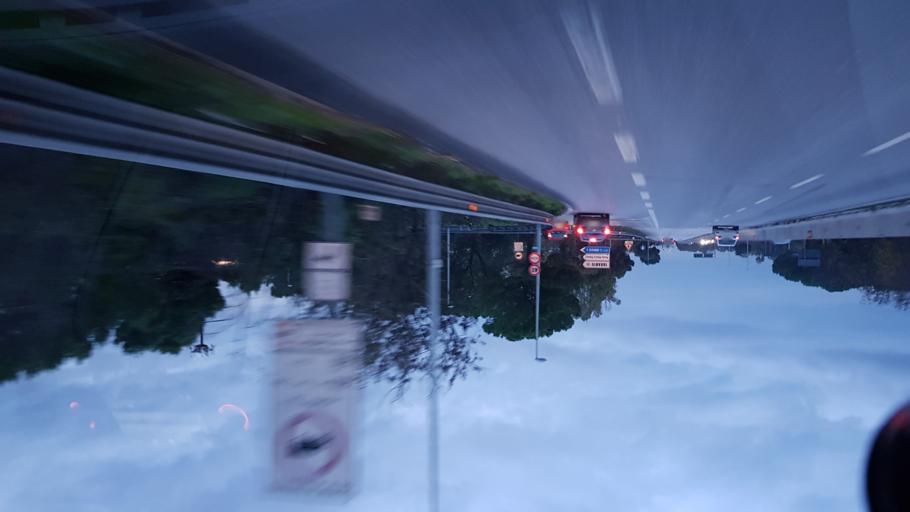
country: IT
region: Apulia
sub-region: Provincia di Taranto
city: Paolo VI
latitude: 40.5053
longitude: 17.2640
